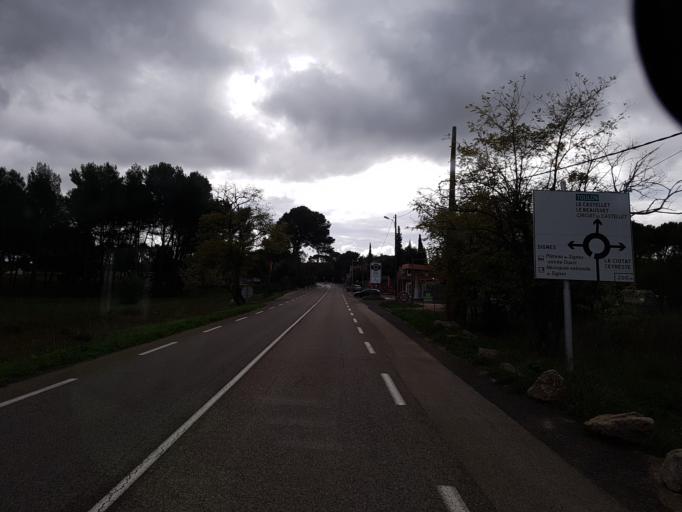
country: FR
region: Provence-Alpes-Cote d'Azur
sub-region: Departement des Bouches-du-Rhone
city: Cuges-les-Pins
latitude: 43.2589
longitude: 5.7500
